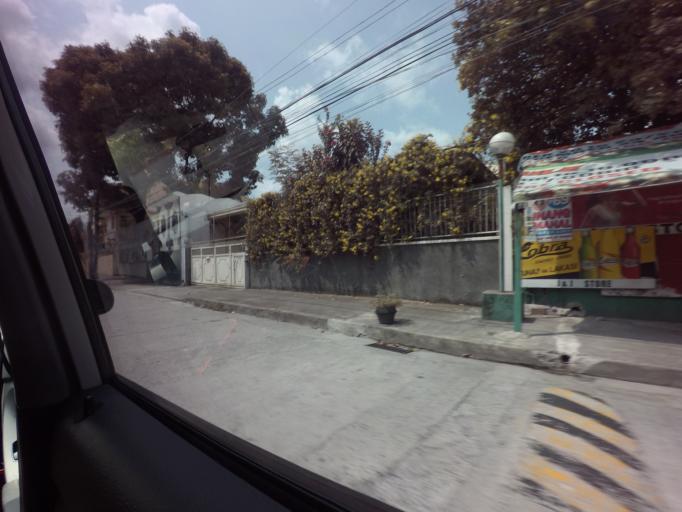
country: PH
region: Metro Manila
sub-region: San Juan
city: San Juan
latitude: 14.5968
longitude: 121.0243
